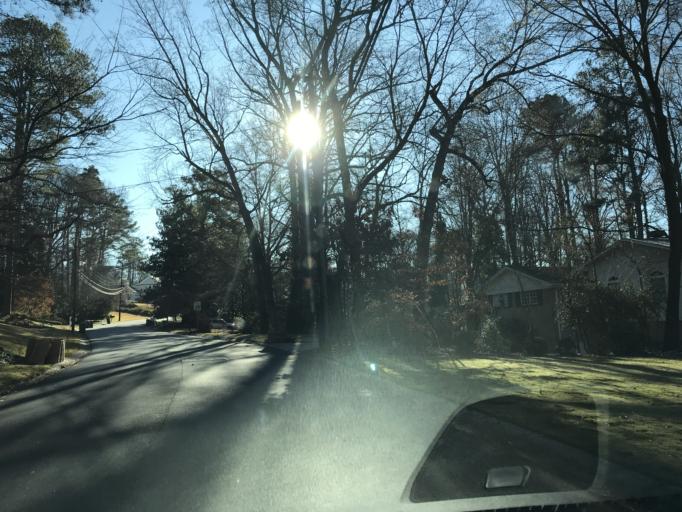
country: US
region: Georgia
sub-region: DeKalb County
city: North Atlanta
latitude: 33.8873
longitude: -84.3423
